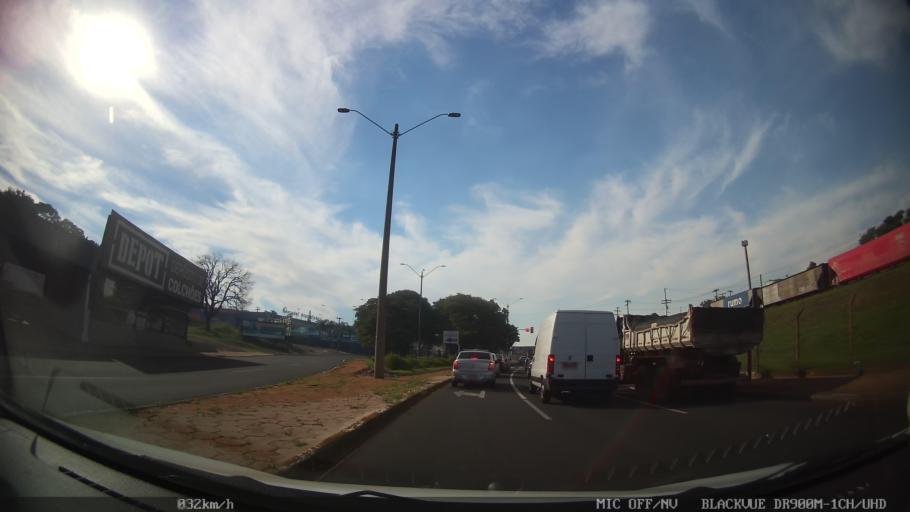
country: BR
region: Sao Paulo
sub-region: Araraquara
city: Araraquara
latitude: -21.7825
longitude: -48.1715
